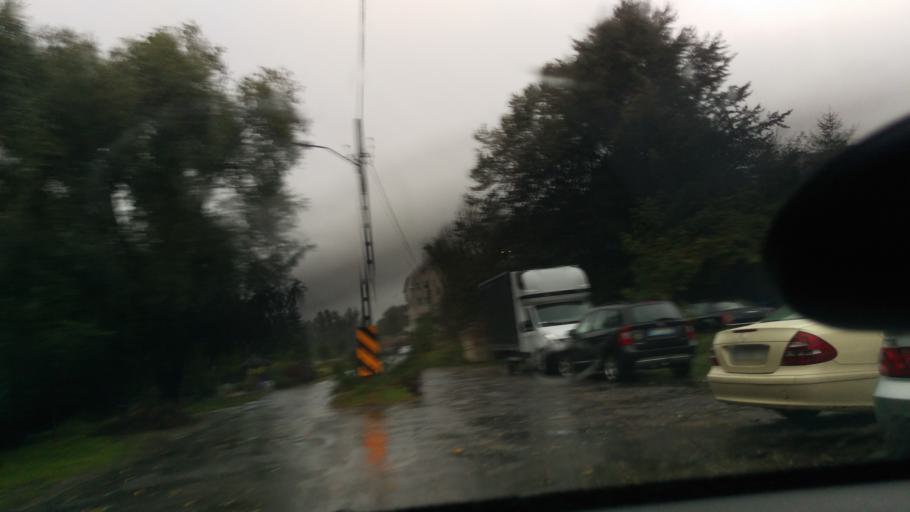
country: PL
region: West Pomeranian Voivodeship
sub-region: Szczecin
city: Szczecin
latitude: 53.3950
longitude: 14.6634
